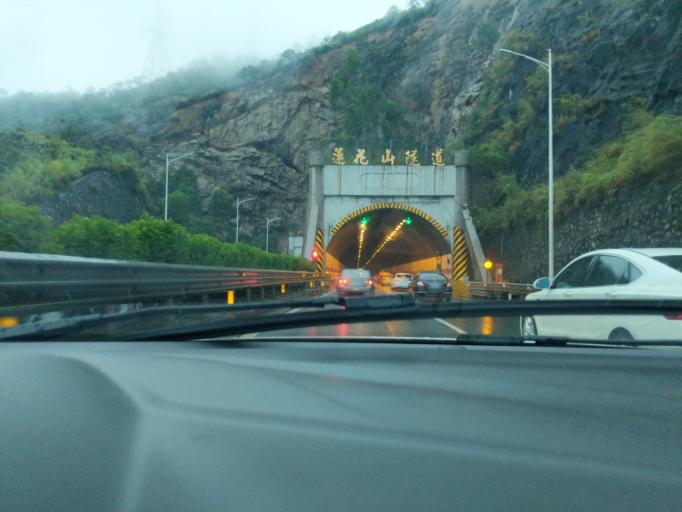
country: CN
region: Guangdong
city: Canghou
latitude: 22.5818
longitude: 113.0349
